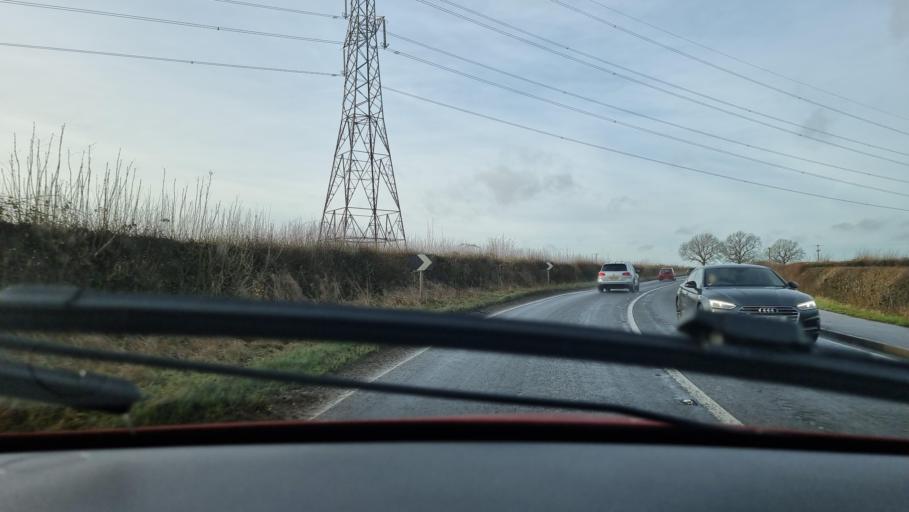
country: GB
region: England
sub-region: Buckinghamshire
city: Steeple Claydon
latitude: 51.9633
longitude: -0.9405
